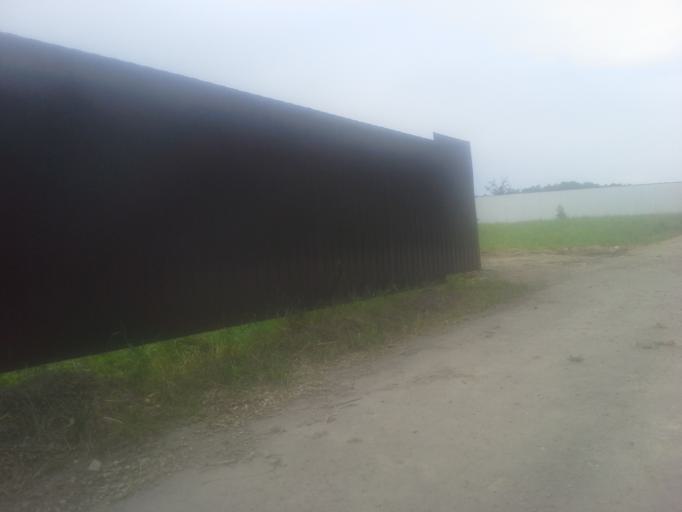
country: RU
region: Moskovskaya
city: Kievskij
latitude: 55.4563
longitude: 36.8839
